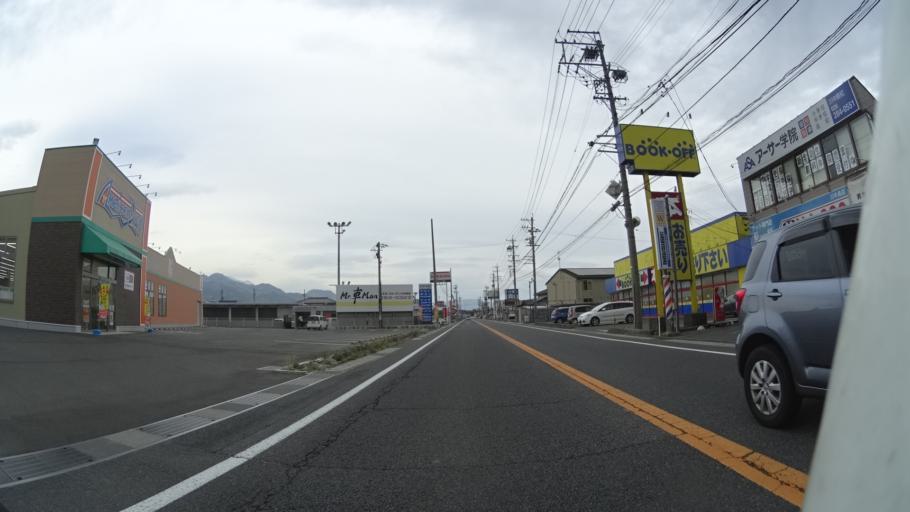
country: JP
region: Nagano
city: Nagano-shi
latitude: 36.6003
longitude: 138.1594
